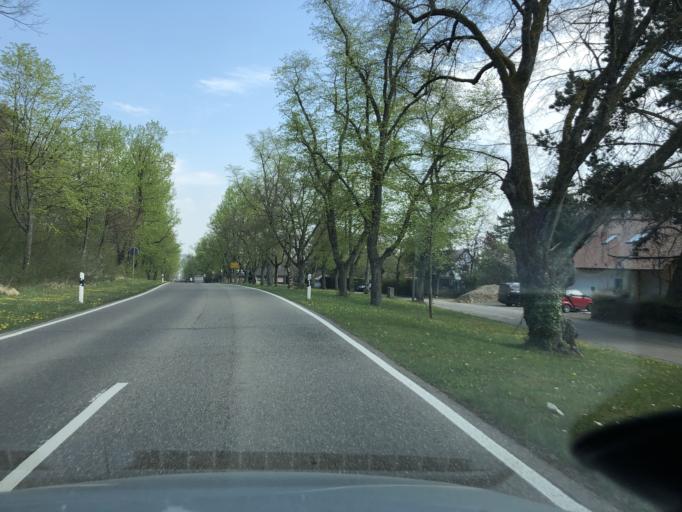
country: DE
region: Baden-Wuerttemberg
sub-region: Regierungsbezirk Stuttgart
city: Weil der Stadt
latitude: 48.7537
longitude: 8.8563
